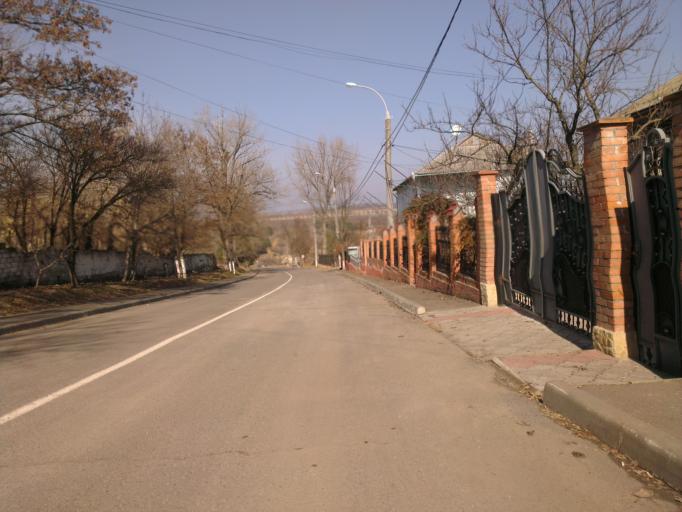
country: MD
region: Chisinau
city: Cricova
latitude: 47.1450
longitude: 28.8637
